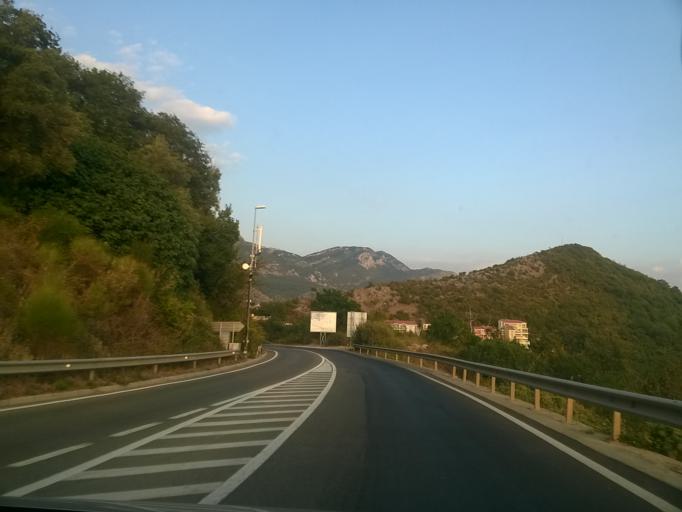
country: ME
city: Petrovac na Moru
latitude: 42.2036
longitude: 18.9524
